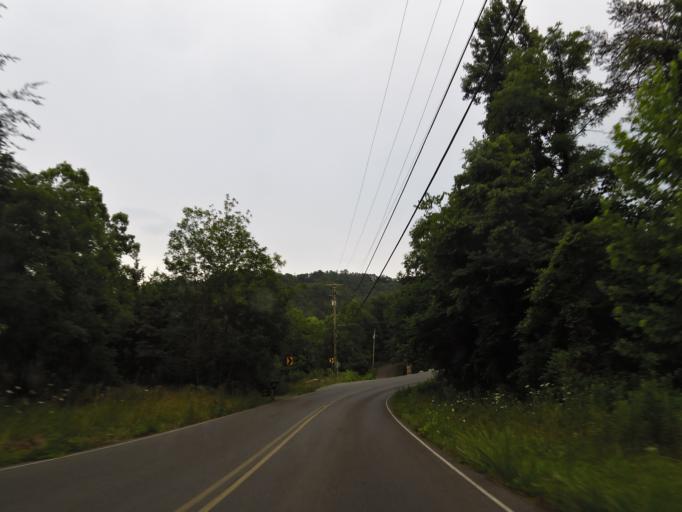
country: US
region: Tennessee
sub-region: Sevier County
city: Pigeon Forge
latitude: 35.7634
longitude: -83.6648
